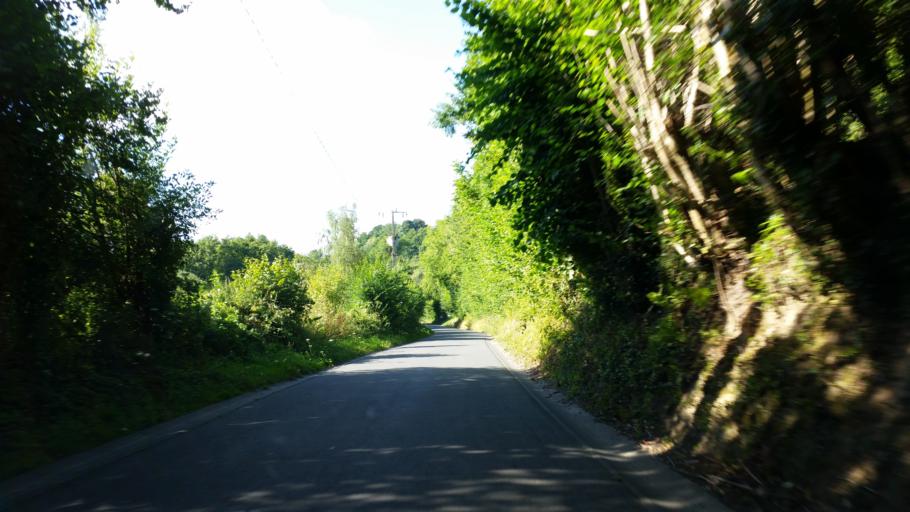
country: FR
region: Lower Normandy
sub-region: Departement du Calvados
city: Equemauville
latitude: 49.3912
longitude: 0.2271
